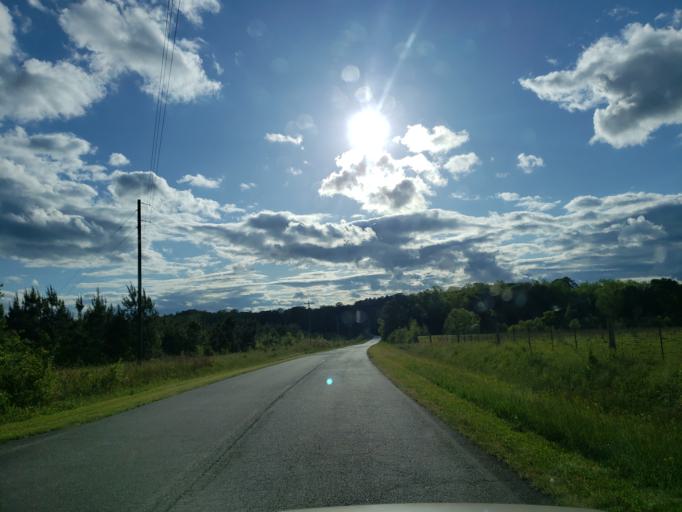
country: US
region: Georgia
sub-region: Haralson County
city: Tallapoosa
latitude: 33.7843
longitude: -85.3038
